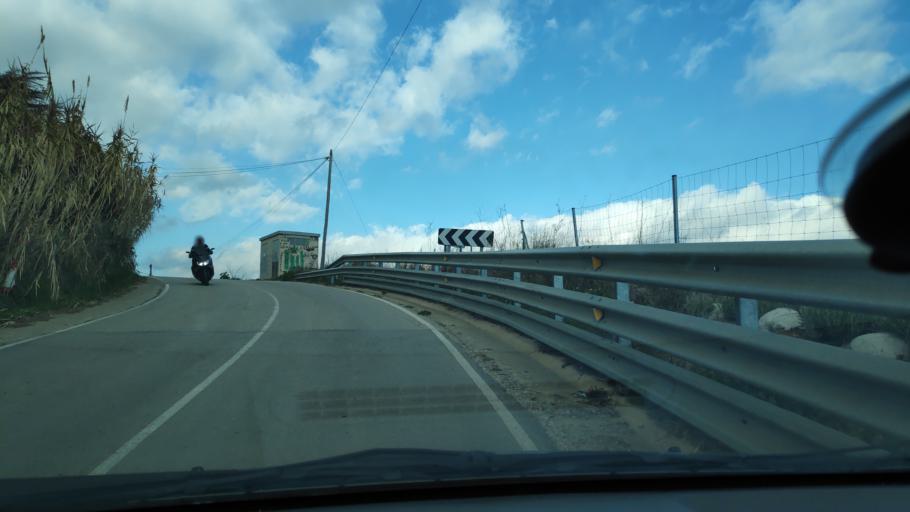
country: ES
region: Catalonia
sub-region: Provincia de Barcelona
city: Terrassa
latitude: 41.5714
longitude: 1.9897
